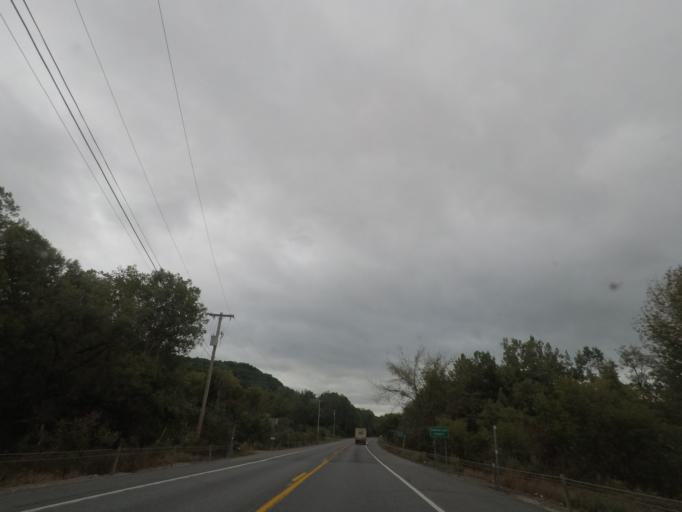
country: US
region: New York
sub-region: Rensselaer County
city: Hoosick Falls
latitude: 42.9439
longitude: -73.3681
